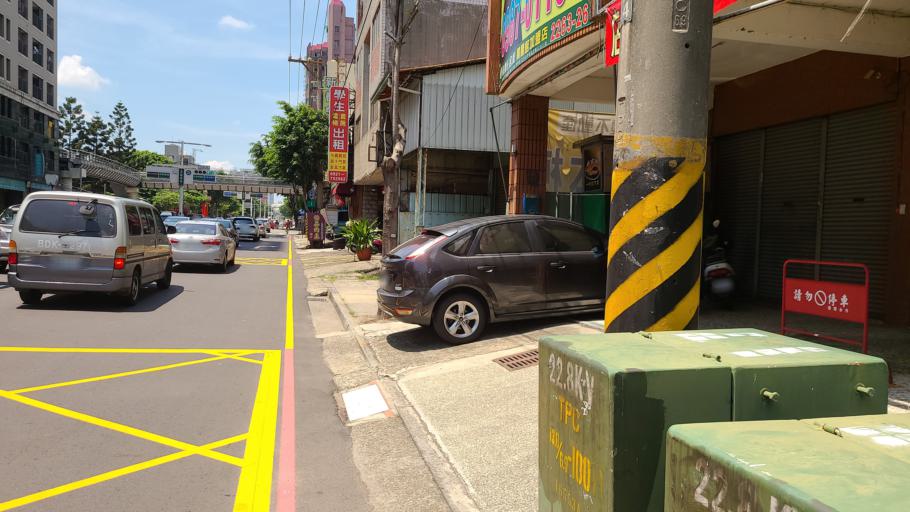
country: TW
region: Taiwan
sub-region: Taichung City
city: Taichung
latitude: 24.1182
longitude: 120.6702
